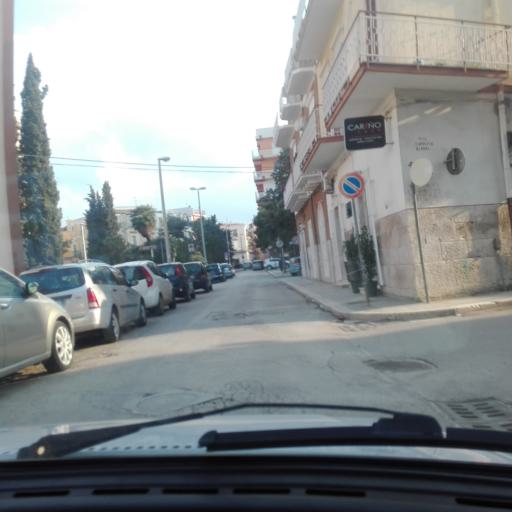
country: IT
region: Apulia
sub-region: Provincia di Bari
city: Corato
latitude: 41.1575
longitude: 16.4098
